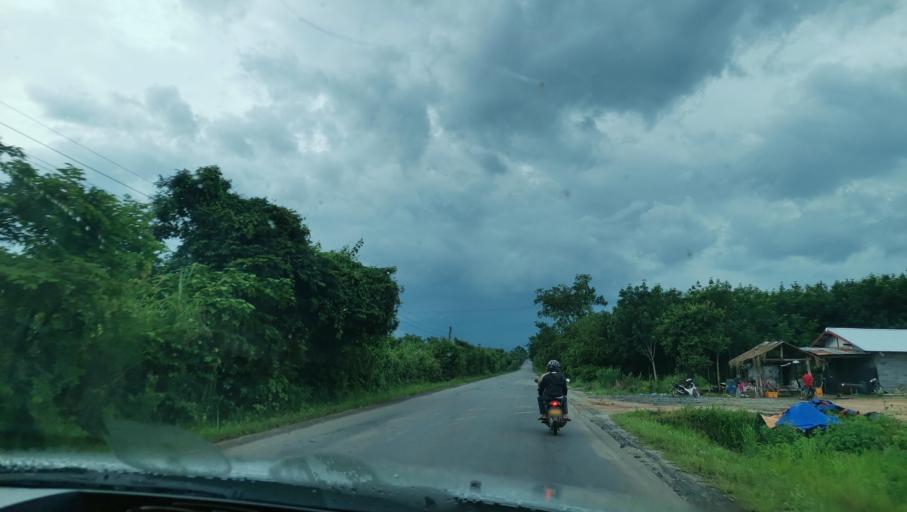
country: TH
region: Nakhon Phanom
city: Ban Phaeng
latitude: 17.8555
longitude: 104.4305
